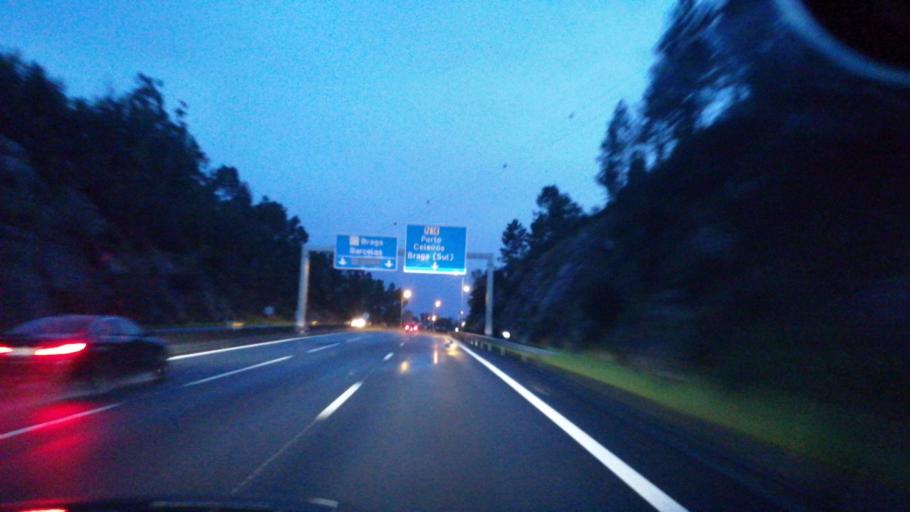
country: PT
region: Braga
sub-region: Braga
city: Oliveira
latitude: 41.5127
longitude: -8.4443
